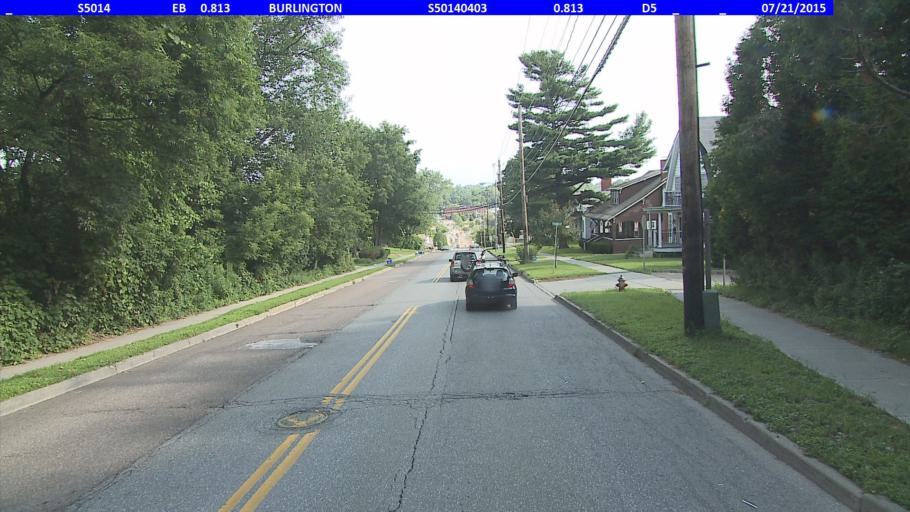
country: US
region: Vermont
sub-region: Chittenden County
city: Winooski
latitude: 44.4853
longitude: -73.1872
